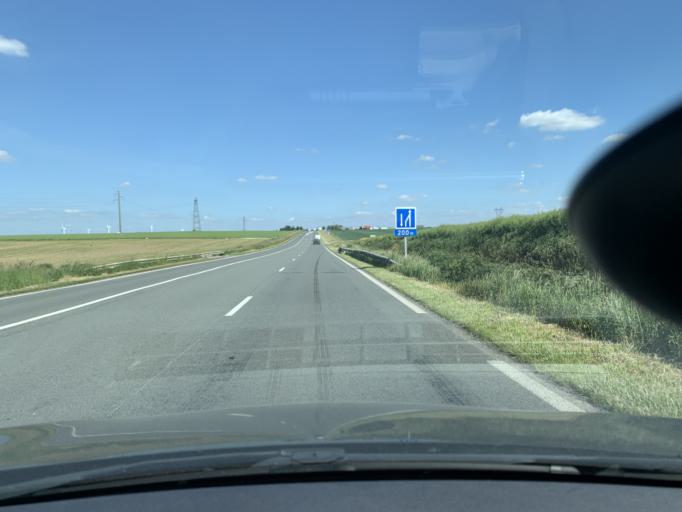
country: FR
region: Nord-Pas-de-Calais
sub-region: Departement du Nord
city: Beauvois-en-Cambresis
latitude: 50.1473
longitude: 3.3540
